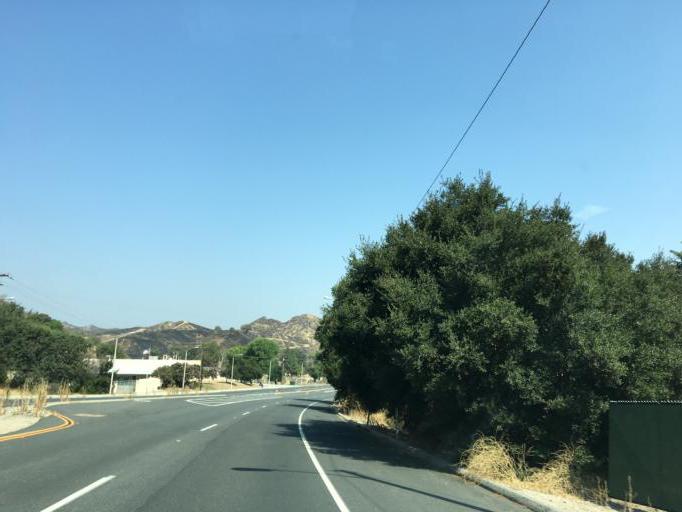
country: US
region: California
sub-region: Los Angeles County
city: Santa Clarita
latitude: 34.3549
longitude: -118.5526
